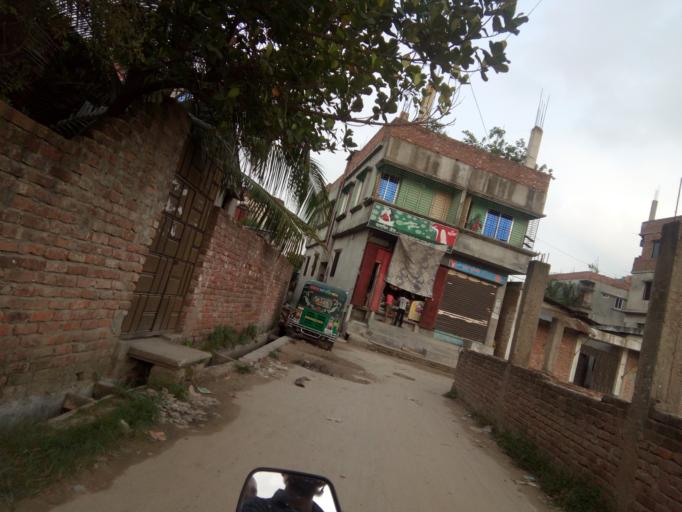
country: BD
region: Dhaka
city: Paltan
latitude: 23.7101
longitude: 90.4643
